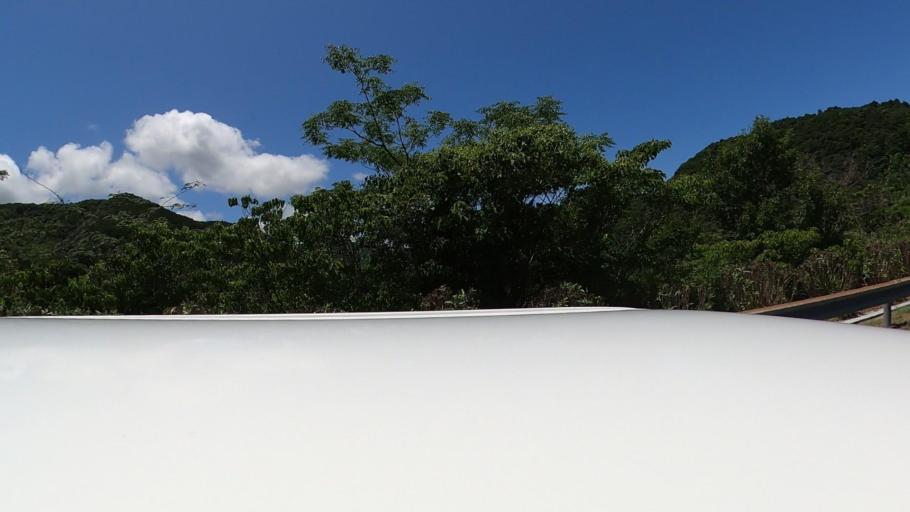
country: JP
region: Miyazaki
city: Nobeoka
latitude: 32.5227
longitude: 131.6650
